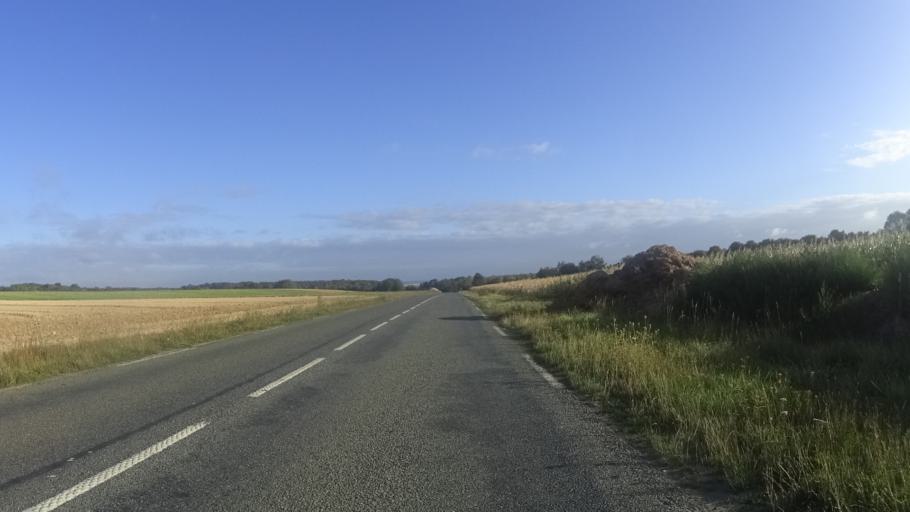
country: FR
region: Picardie
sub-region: Departement de l'Oise
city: Pontpoint
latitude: 49.2818
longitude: 2.6921
